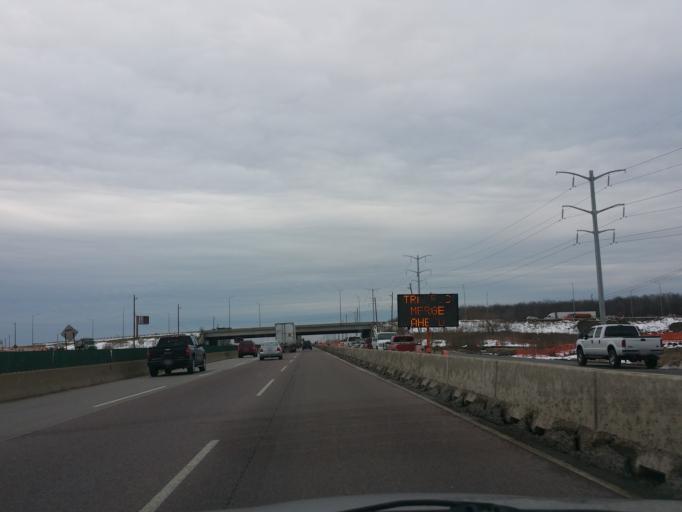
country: US
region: Illinois
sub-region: Cook County
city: Streamwood
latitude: 42.0664
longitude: -88.1973
